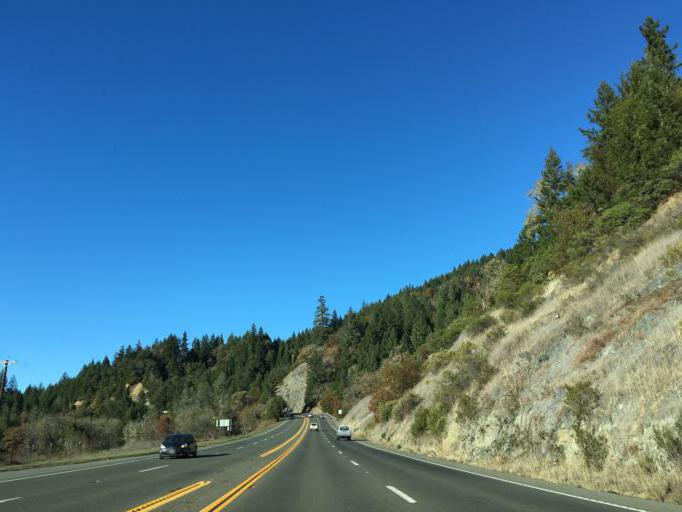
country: US
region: California
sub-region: Mendocino County
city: Brooktrails
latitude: 39.5190
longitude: -123.3918
